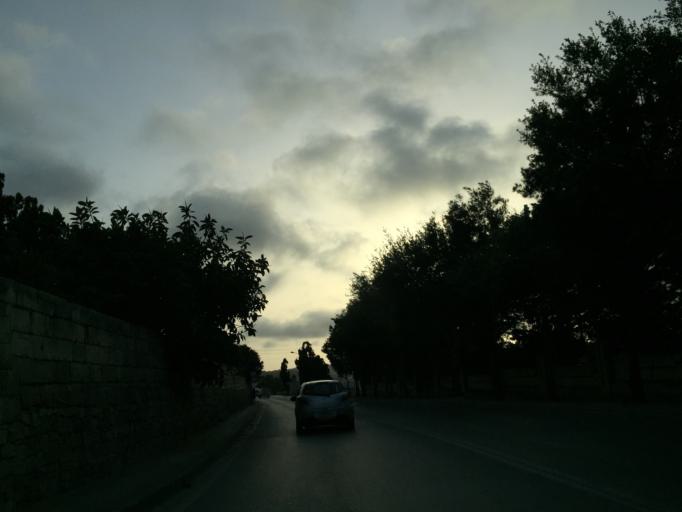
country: MT
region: Il-Mosta
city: Mosta
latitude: 35.9174
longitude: 14.4160
